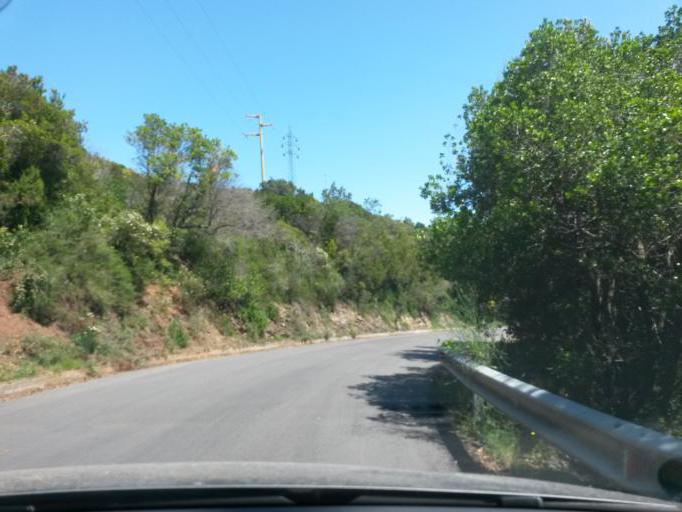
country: IT
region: Tuscany
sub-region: Provincia di Livorno
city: Rio nell'Elba
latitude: 42.8510
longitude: 10.4098
